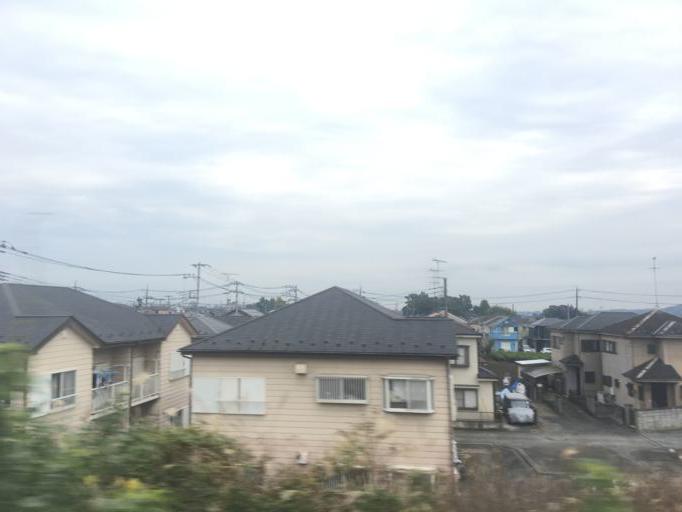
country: JP
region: Saitama
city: Hanno
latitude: 35.8422
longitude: 139.3338
